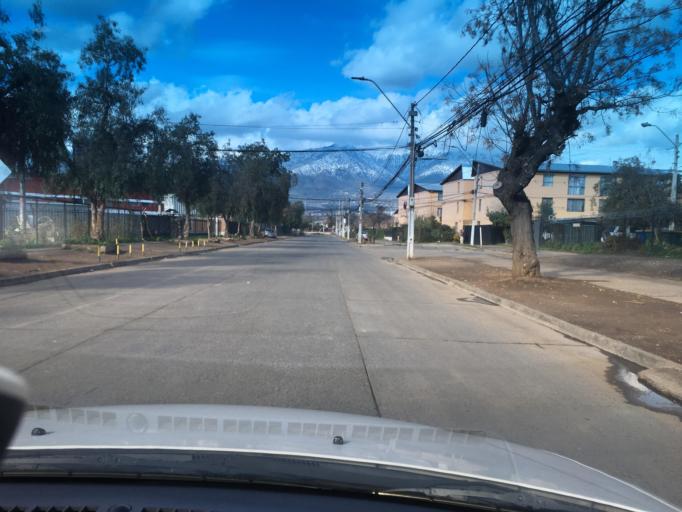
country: CL
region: Santiago Metropolitan
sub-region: Provincia de Santiago
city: Villa Presidente Frei, Nunoa, Santiago, Chile
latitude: -33.5158
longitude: -70.5867
